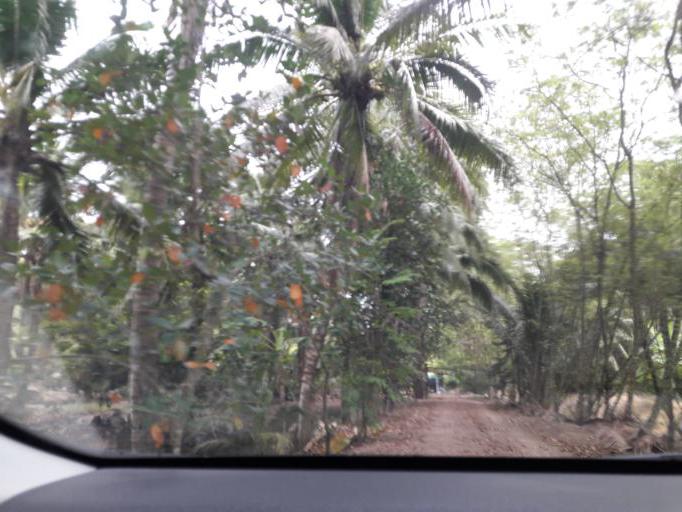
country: TH
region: Ratchaburi
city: Damnoen Saduak
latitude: 13.5678
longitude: 99.9781
